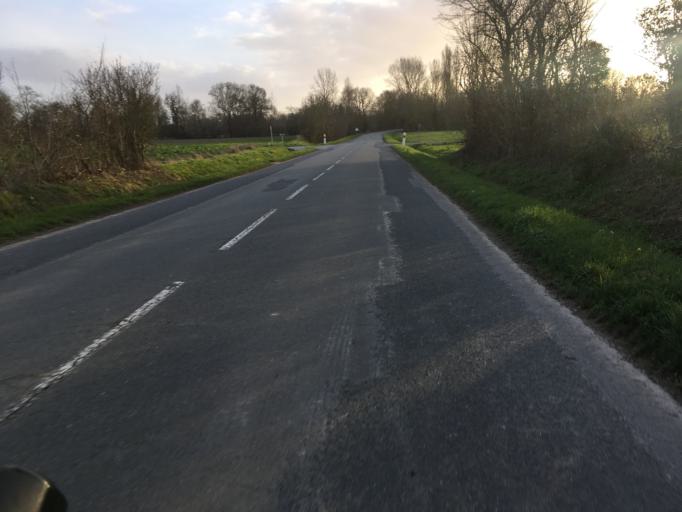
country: FR
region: Poitou-Charentes
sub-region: Departement de la Charente-Maritime
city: Courcon
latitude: 46.1708
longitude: -0.8490
